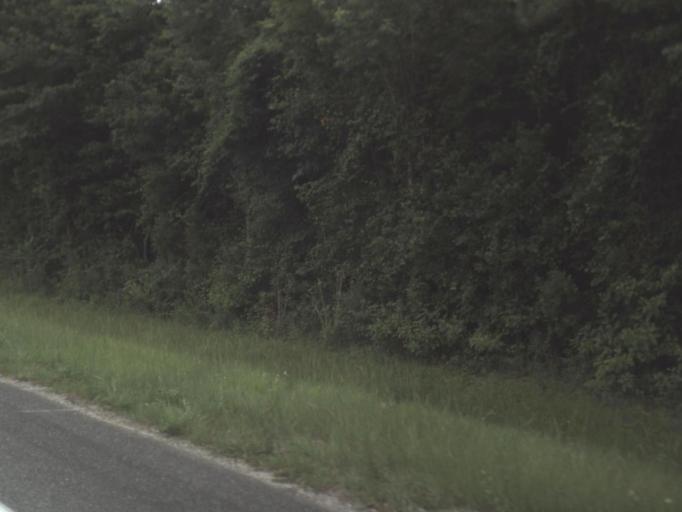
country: US
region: Florida
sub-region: Union County
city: Lake Butler
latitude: 30.0294
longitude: -82.3614
